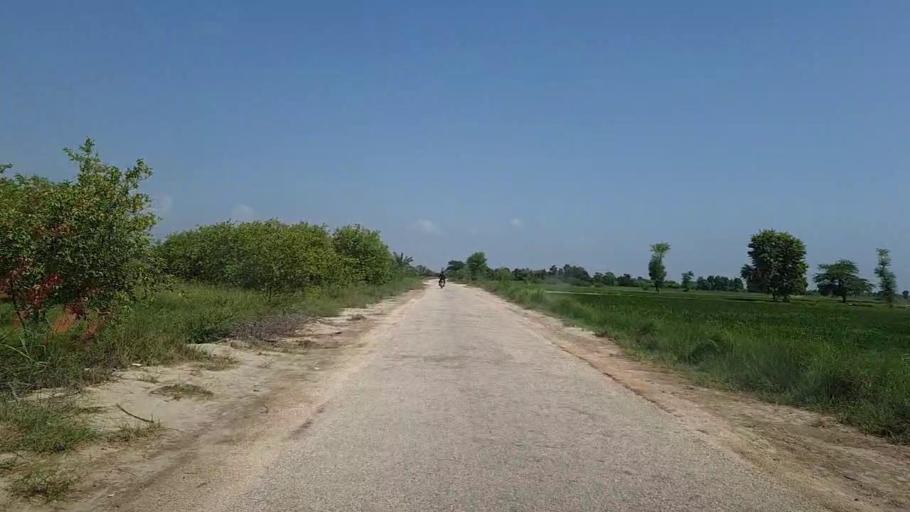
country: PK
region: Sindh
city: Bhiria
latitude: 26.8972
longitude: 68.2188
